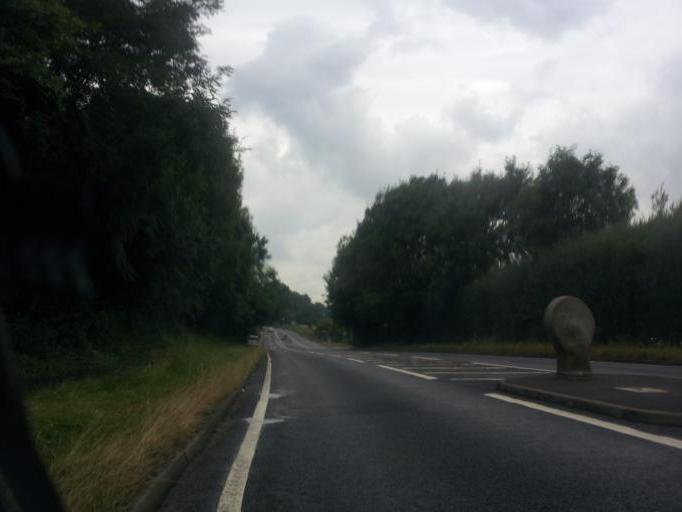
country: GB
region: England
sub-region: Kent
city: West Malling
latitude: 51.3023
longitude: 0.3945
